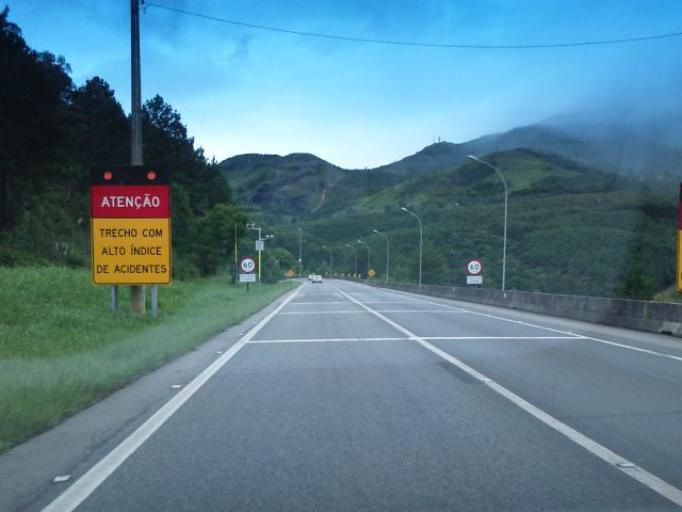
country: BR
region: Parana
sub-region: Campina Grande Do Sul
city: Campina Grande do Sul
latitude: -25.1152
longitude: -48.8495
